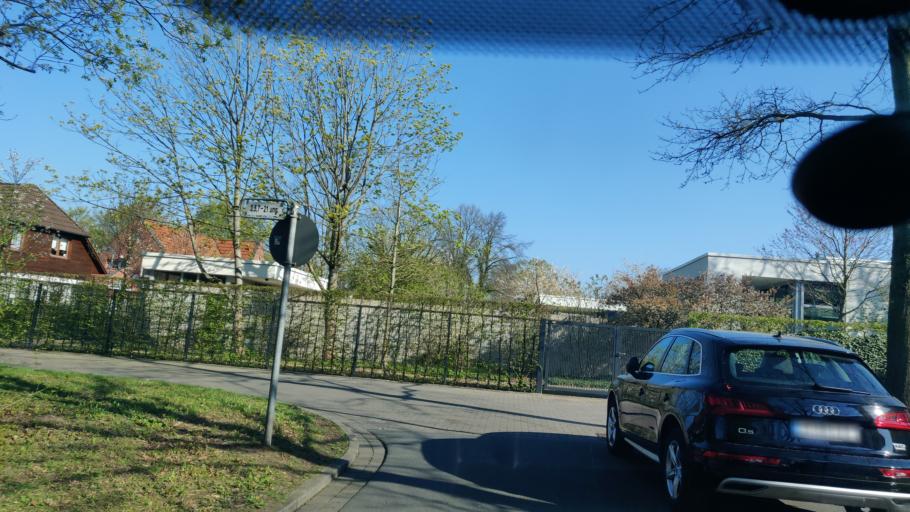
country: DE
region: Lower Saxony
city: Laatzen
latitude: 52.3604
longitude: 9.8174
